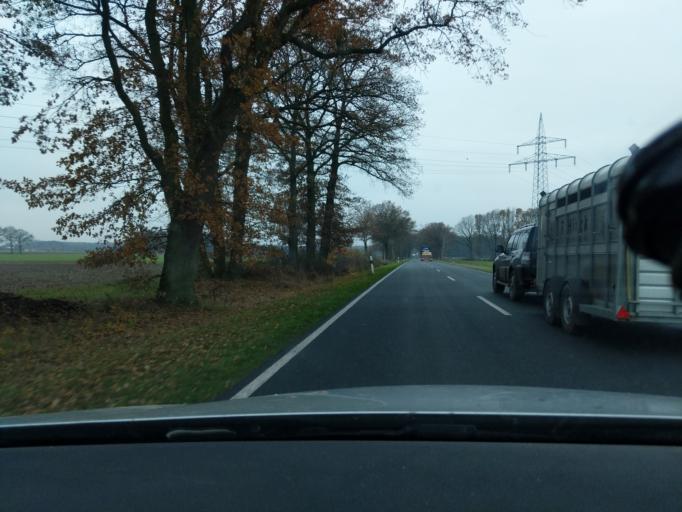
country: DE
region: Lower Saxony
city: Heeslingen
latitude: 53.3057
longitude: 9.3173
